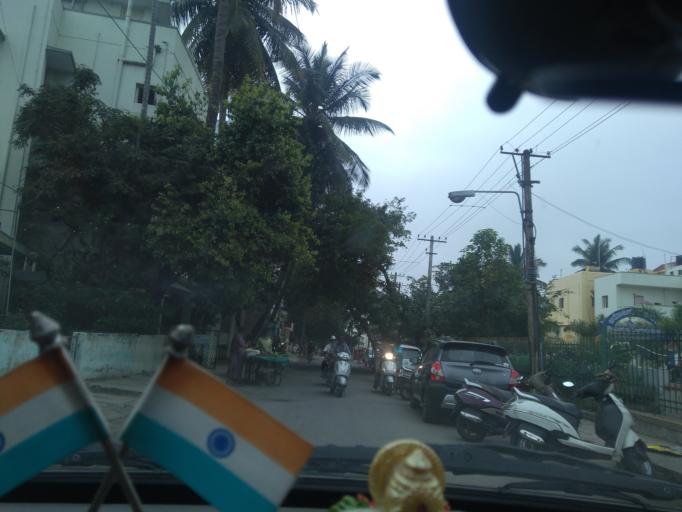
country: IN
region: Karnataka
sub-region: Bangalore Urban
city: Bangalore
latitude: 12.9873
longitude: 77.5506
